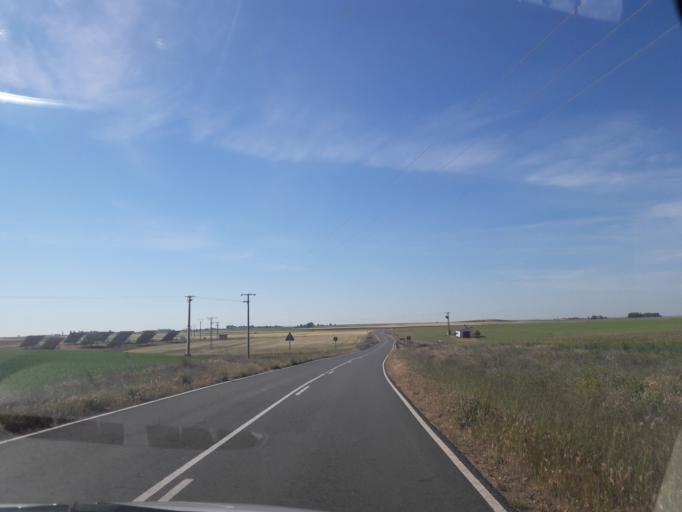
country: ES
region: Castille and Leon
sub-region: Provincia de Salamanca
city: Espino de la Orbada
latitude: 41.1010
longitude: -5.4186
